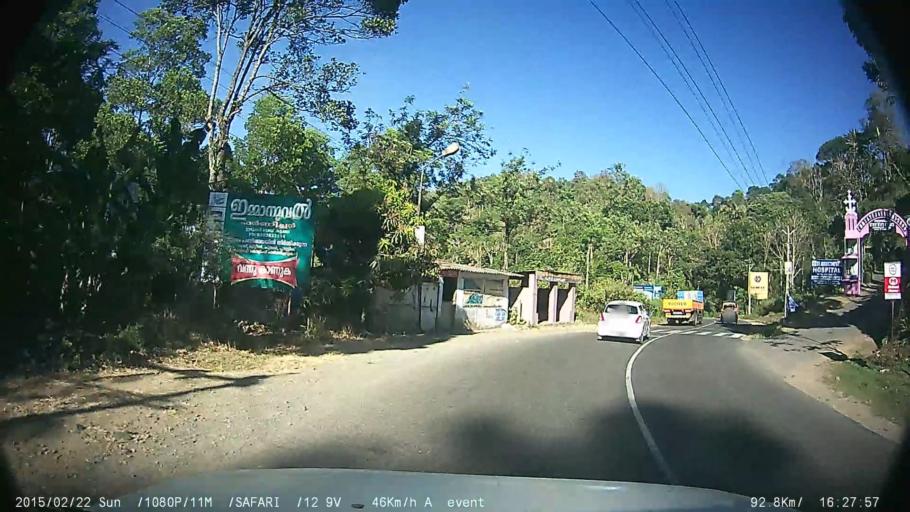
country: IN
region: Tamil Nadu
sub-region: Theni
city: Gudalur
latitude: 9.6077
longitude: 77.1450
